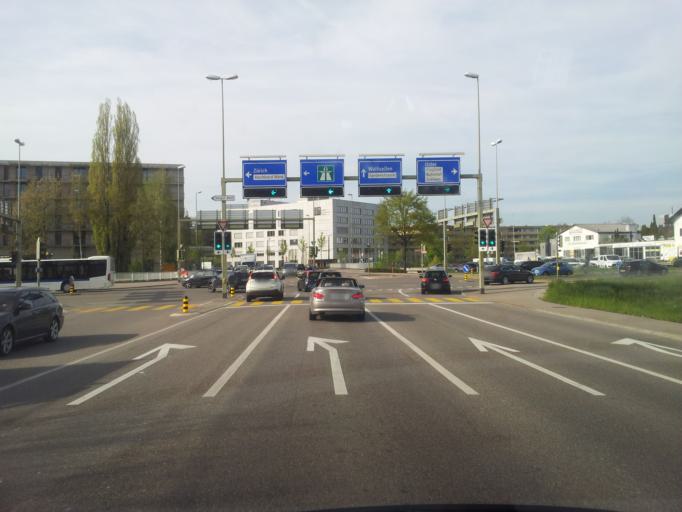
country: CH
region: Zurich
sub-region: Bezirk Uster
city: Duebendorf / Wasserfurren
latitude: 47.4023
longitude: 8.6062
